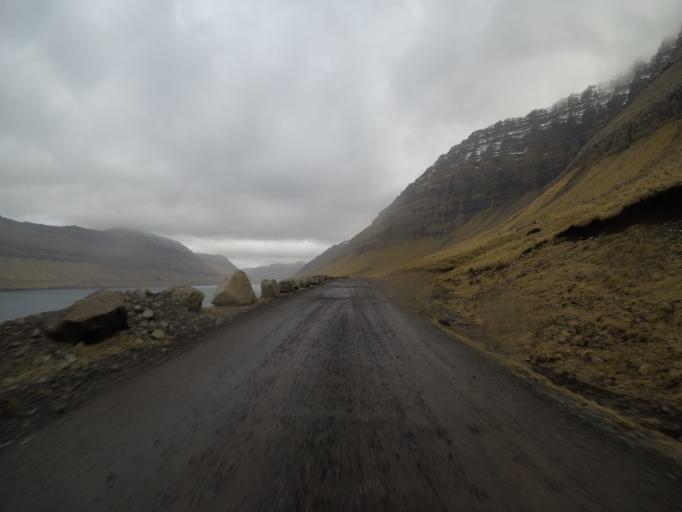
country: FO
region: Nordoyar
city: Klaksvik
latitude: 62.3379
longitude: -6.5788
